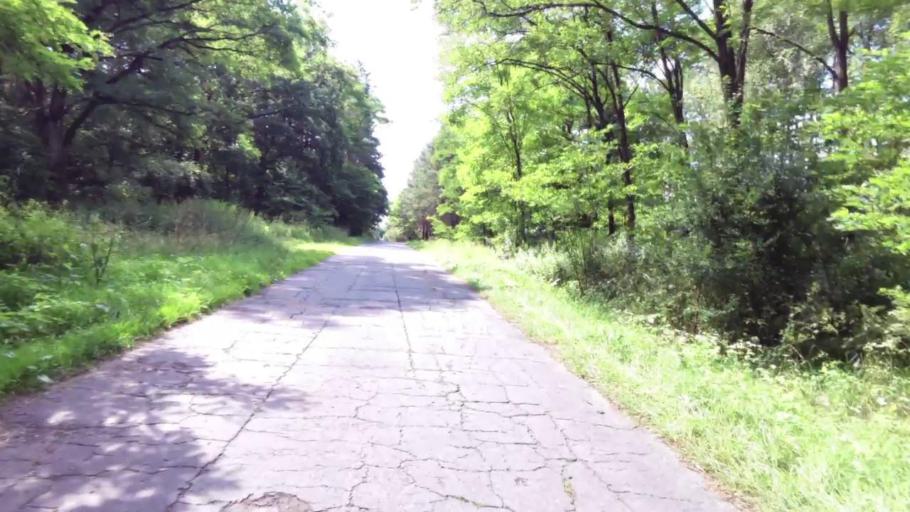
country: PL
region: West Pomeranian Voivodeship
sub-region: Powiat stargardzki
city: Dobrzany
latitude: 53.3778
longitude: 15.3738
